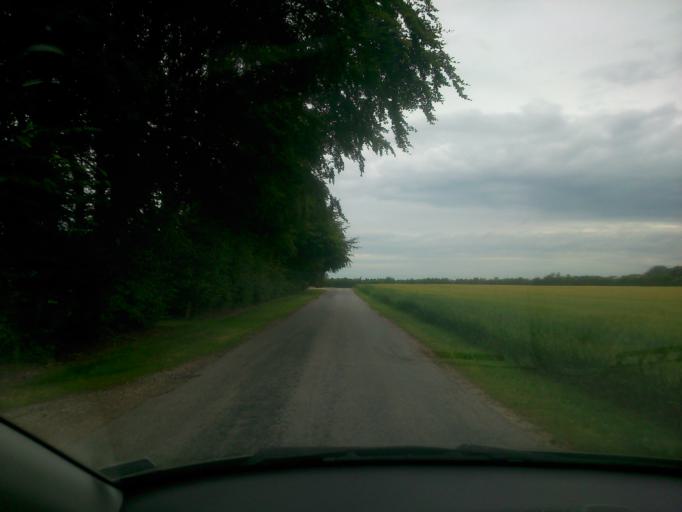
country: DK
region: South Denmark
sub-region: Esbjerg Kommune
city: Esbjerg
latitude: 55.5497
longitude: 8.4196
